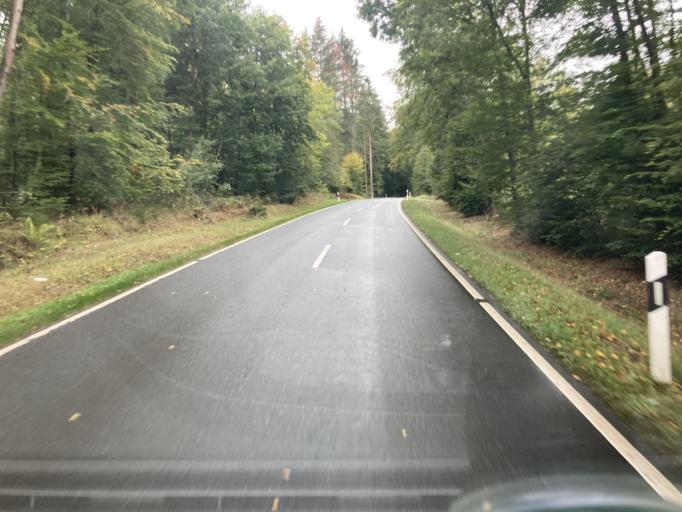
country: DE
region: Hesse
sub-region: Regierungsbezirk Darmstadt
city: Neu-Anspach
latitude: 50.3403
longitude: 8.4928
